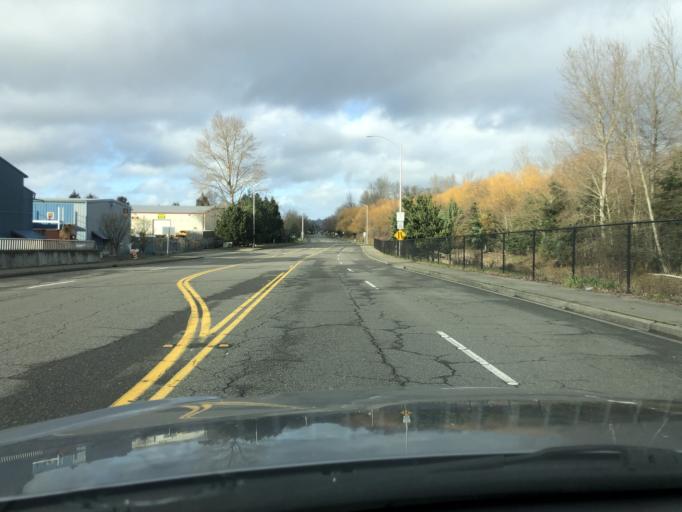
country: US
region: Washington
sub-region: King County
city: Kent
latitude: 47.4271
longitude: -122.2442
